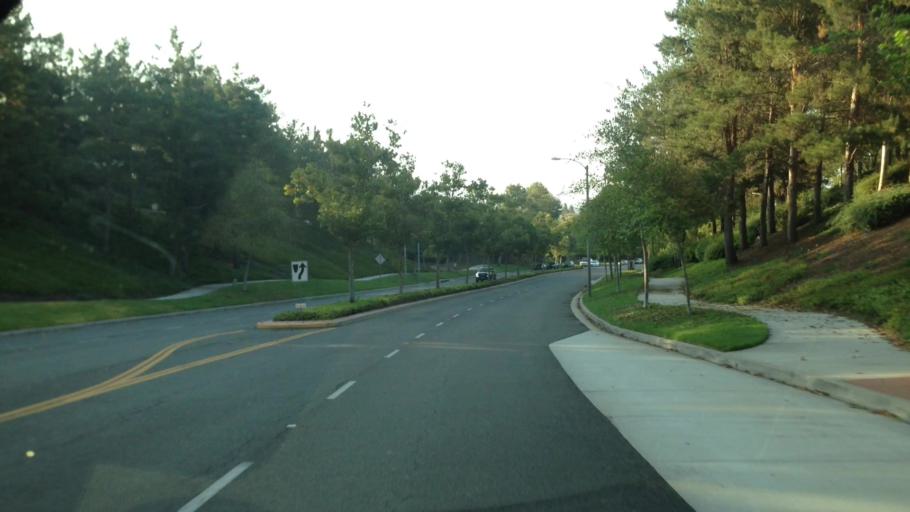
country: US
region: California
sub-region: Orange County
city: Rancho Santa Margarita
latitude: 33.6560
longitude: -117.6138
